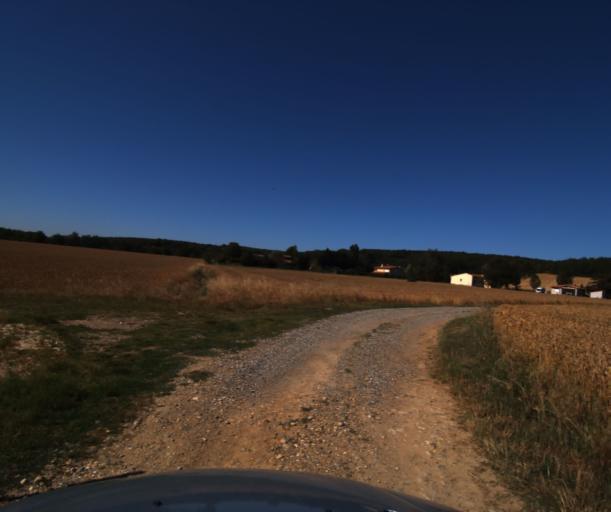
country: FR
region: Midi-Pyrenees
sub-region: Departement de la Haute-Garonne
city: Eaunes
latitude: 43.4140
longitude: 1.3567
